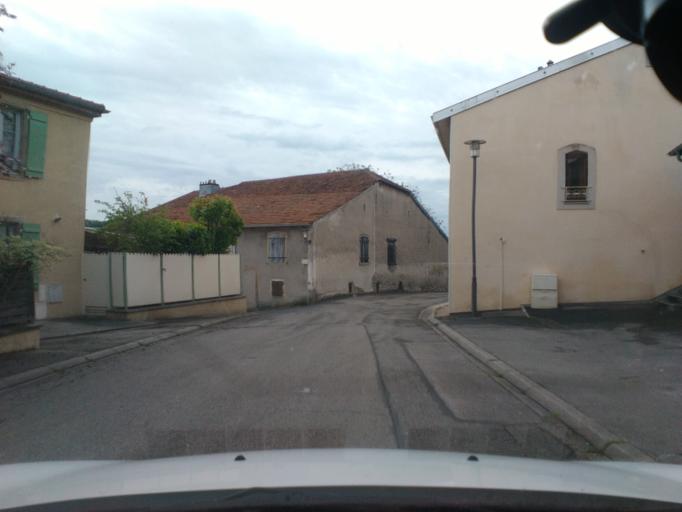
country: FR
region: Lorraine
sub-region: Departement des Vosges
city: Mirecourt
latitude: 48.3212
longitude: 6.1251
